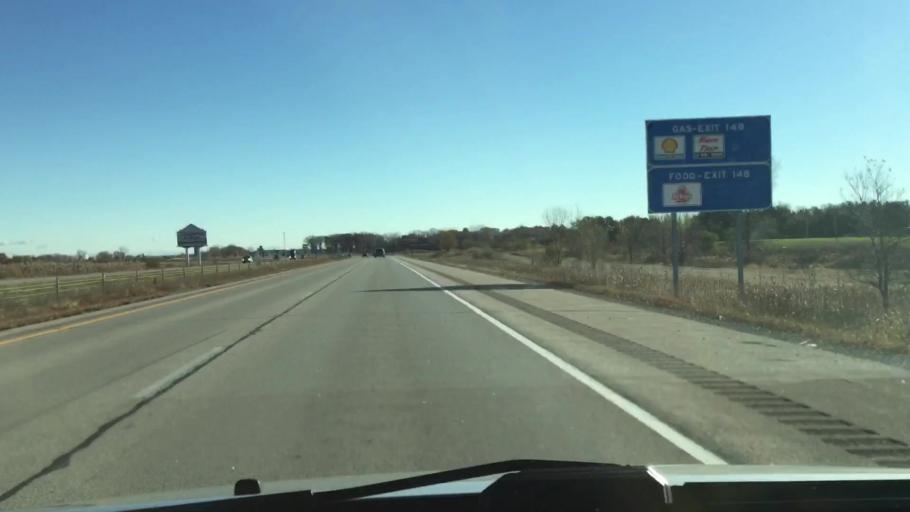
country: US
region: Wisconsin
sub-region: Outagamie County
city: Kaukauna
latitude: 44.2975
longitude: -88.2857
